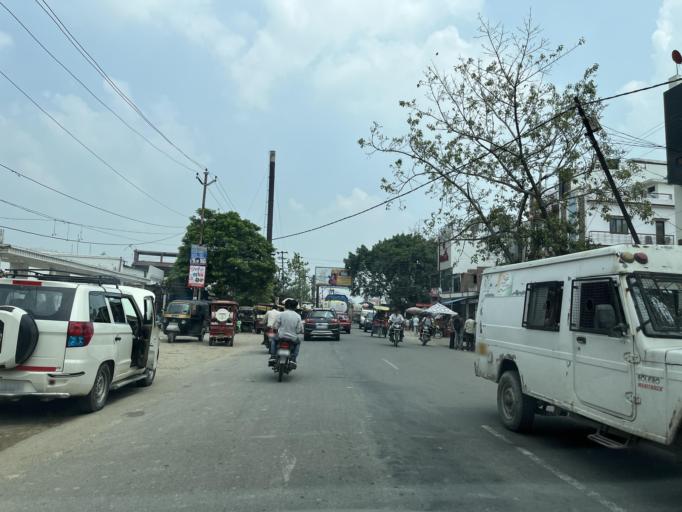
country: IN
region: Uttar Pradesh
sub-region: Bijnor
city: Najibabad
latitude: 29.6018
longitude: 78.3420
